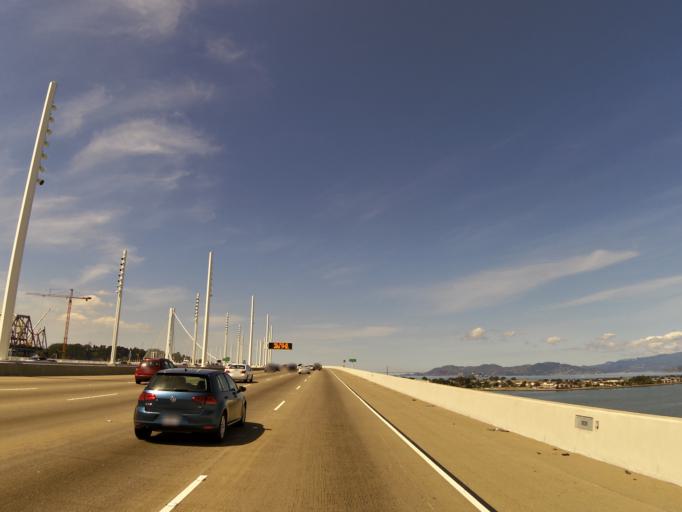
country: US
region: California
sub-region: Alameda County
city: Emeryville
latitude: 37.8194
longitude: -122.3484
